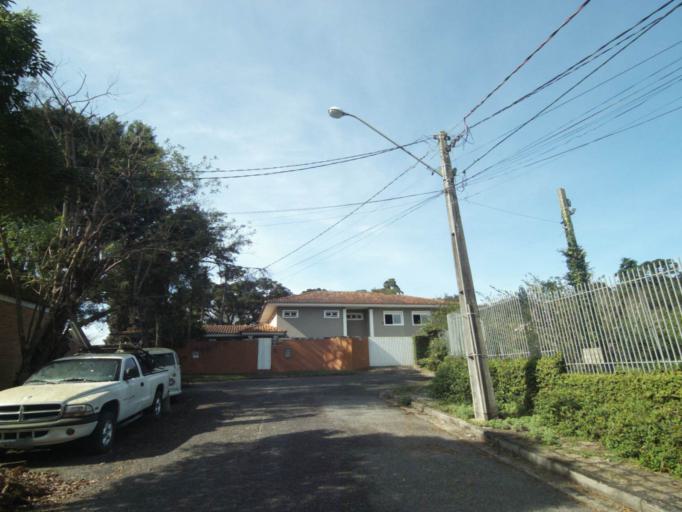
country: BR
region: Parana
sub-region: Curitiba
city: Curitiba
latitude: -25.4162
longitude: -49.2998
